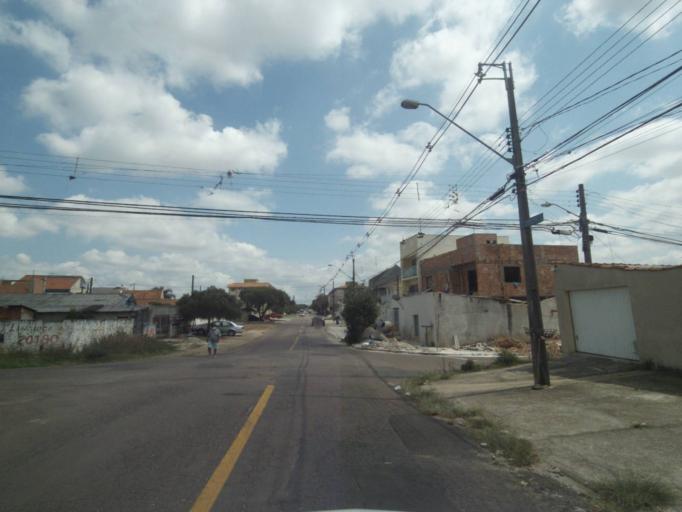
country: BR
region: Parana
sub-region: Sao Jose Dos Pinhais
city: Sao Jose dos Pinhais
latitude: -25.5458
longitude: -49.2499
